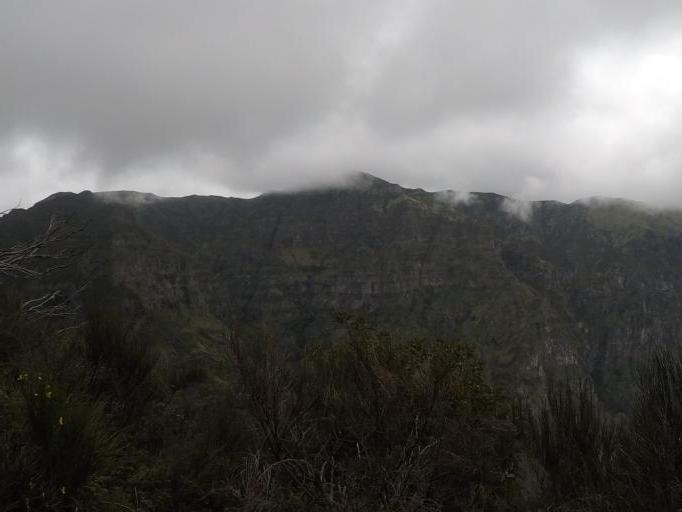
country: PT
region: Madeira
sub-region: Camara de Lobos
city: Curral das Freiras
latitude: 32.7346
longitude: -16.9925
